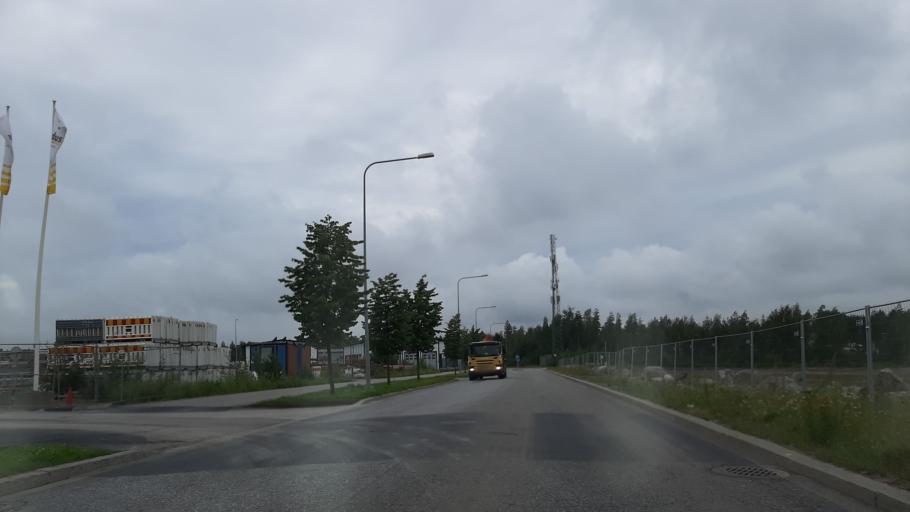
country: FI
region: Uusimaa
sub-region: Helsinki
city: Vantaa
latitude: 60.2408
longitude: 25.0508
